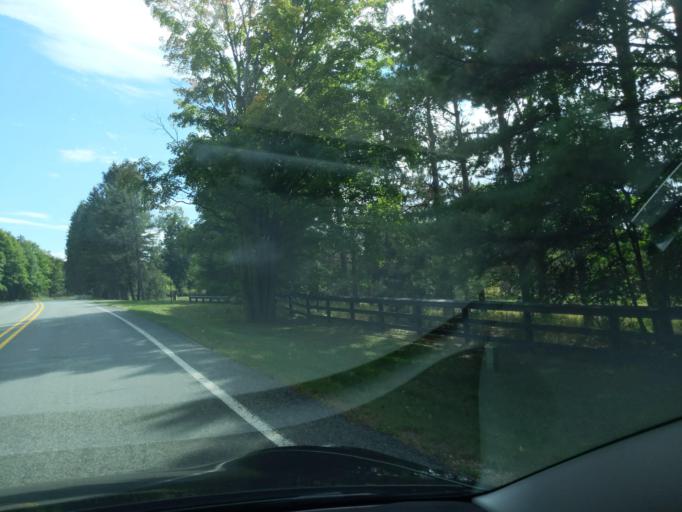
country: US
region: Michigan
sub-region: Antrim County
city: Bellaire
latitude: 44.9845
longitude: -85.2834
